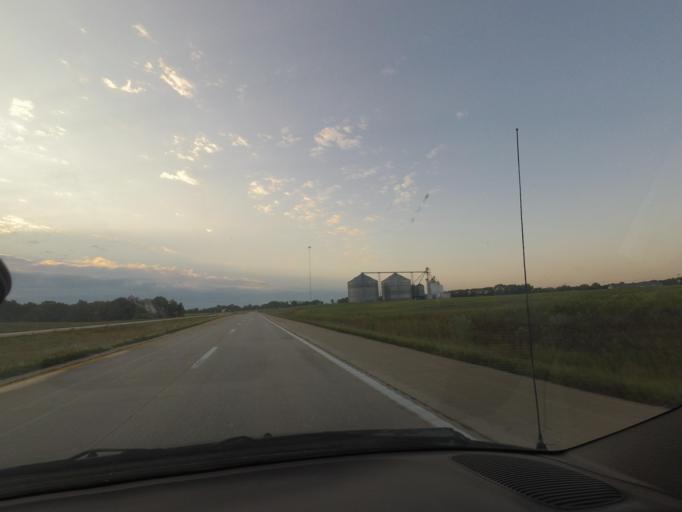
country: US
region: Missouri
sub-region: Shelby County
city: Shelbina
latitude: 39.7460
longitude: -92.2457
